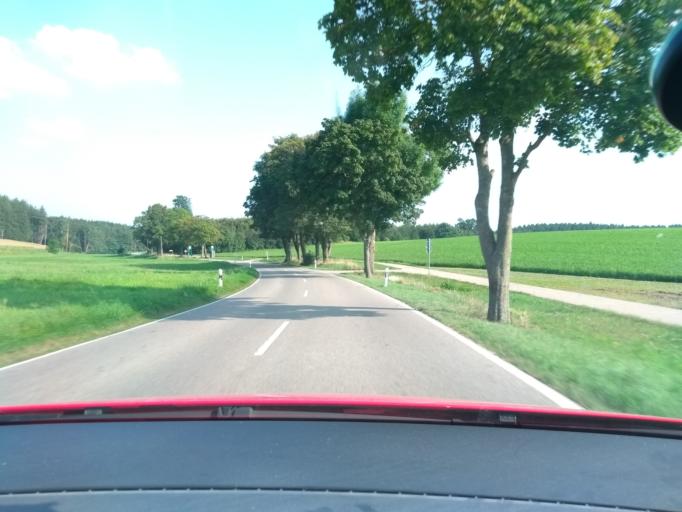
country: DE
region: Bavaria
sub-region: Upper Bavaria
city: Schwabhausen
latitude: 48.3888
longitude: 11.3265
